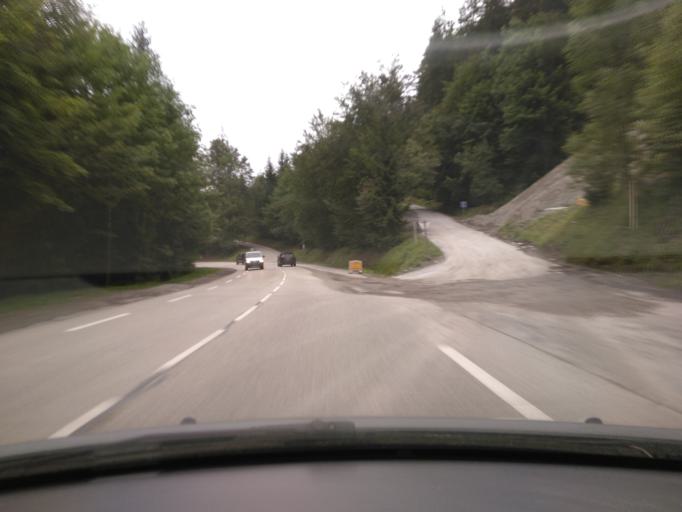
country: FR
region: Rhone-Alpes
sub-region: Departement de la Haute-Savoie
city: La Clusaz
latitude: 45.9105
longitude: 6.4196
